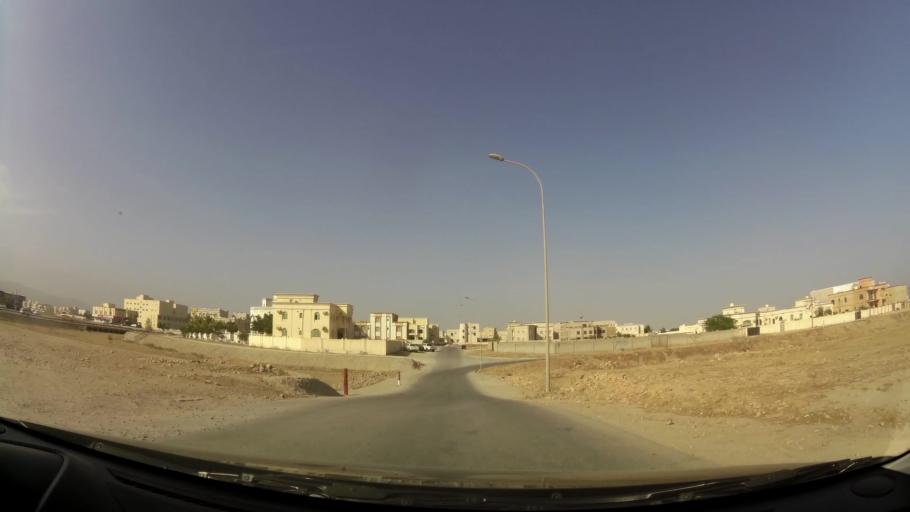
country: OM
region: Zufar
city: Salalah
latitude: 17.0075
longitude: 54.0230
